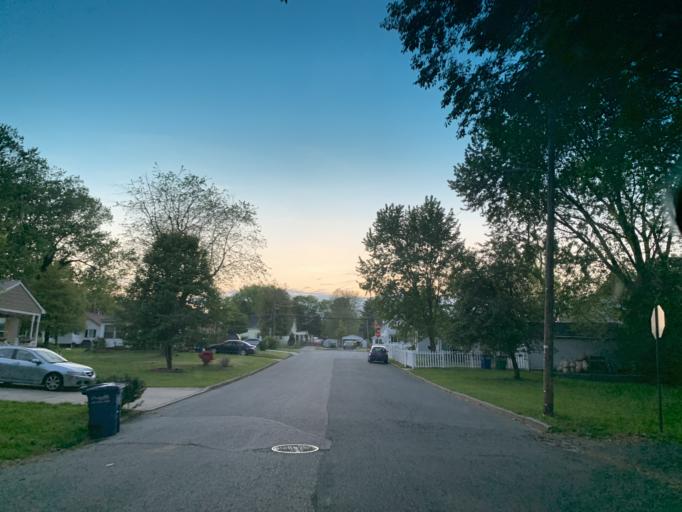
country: US
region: Maryland
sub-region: Harford County
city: Aberdeen
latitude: 39.5058
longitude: -76.1722
